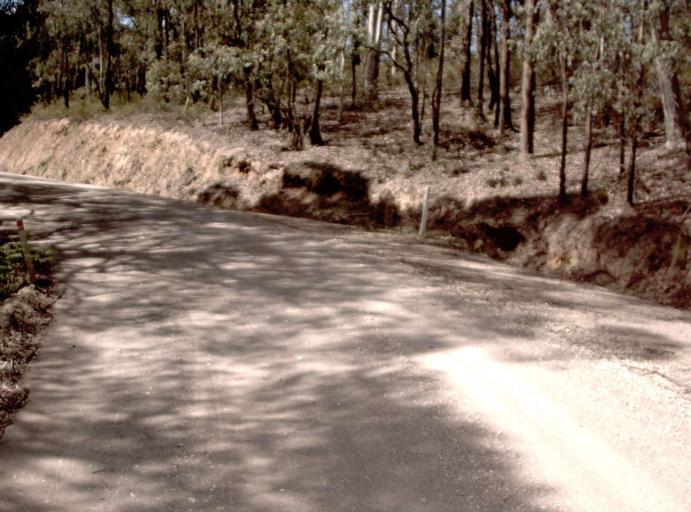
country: AU
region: New South Wales
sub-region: Bombala
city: Bombala
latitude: -37.1848
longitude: 148.7086
